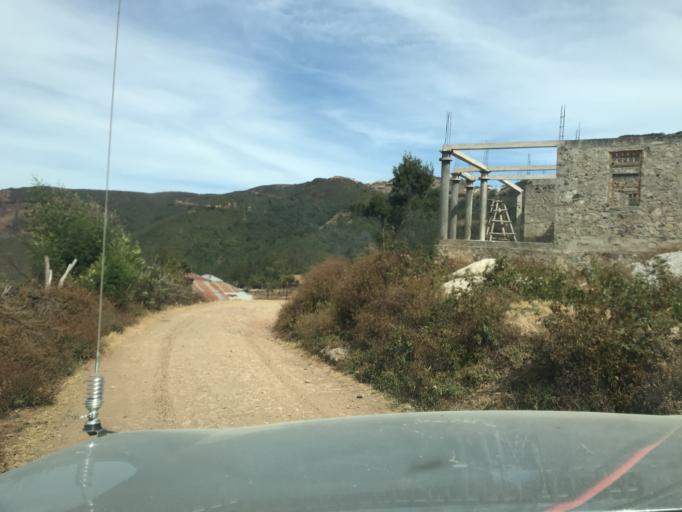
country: TL
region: Ainaro
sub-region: Ainaro
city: Ainaro
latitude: -8.8832
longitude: 125.5346
